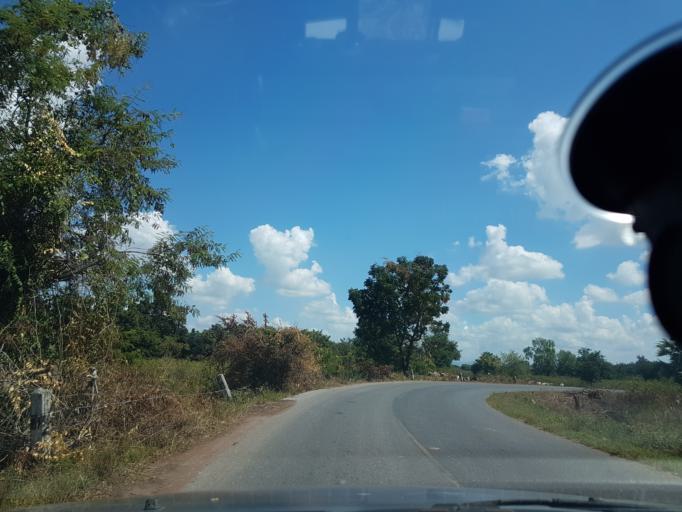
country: TH
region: Lop Buri
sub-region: Amphoe Tha Luang
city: Tha Luang
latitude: 14.9994
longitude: 101.0102
